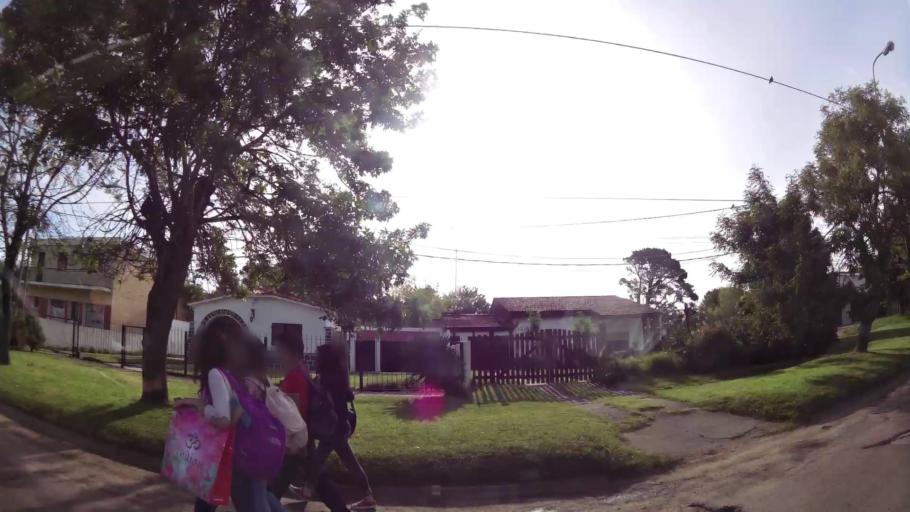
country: UY
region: Canelones
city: Atlantida
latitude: -34.7813
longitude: -55.8387
